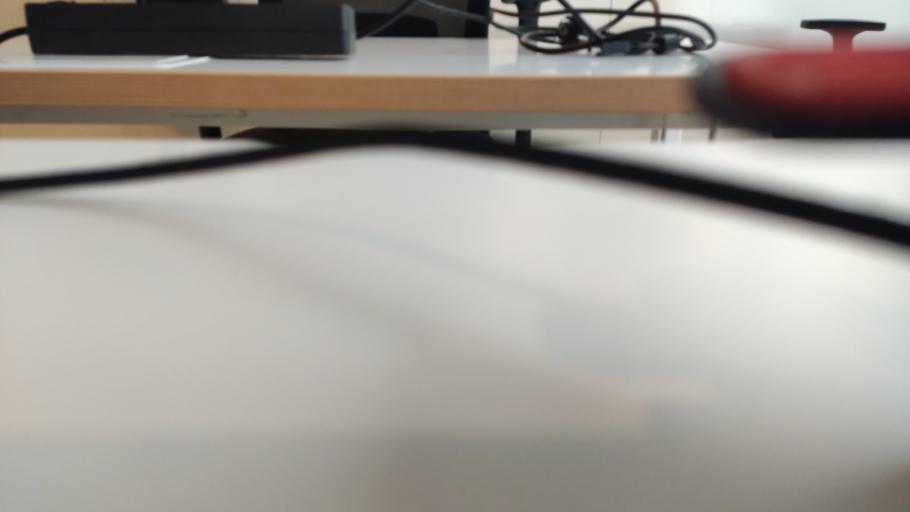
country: RU
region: Moskovskaya
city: Shevlyakovo
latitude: 56.4128
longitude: 36.9265
